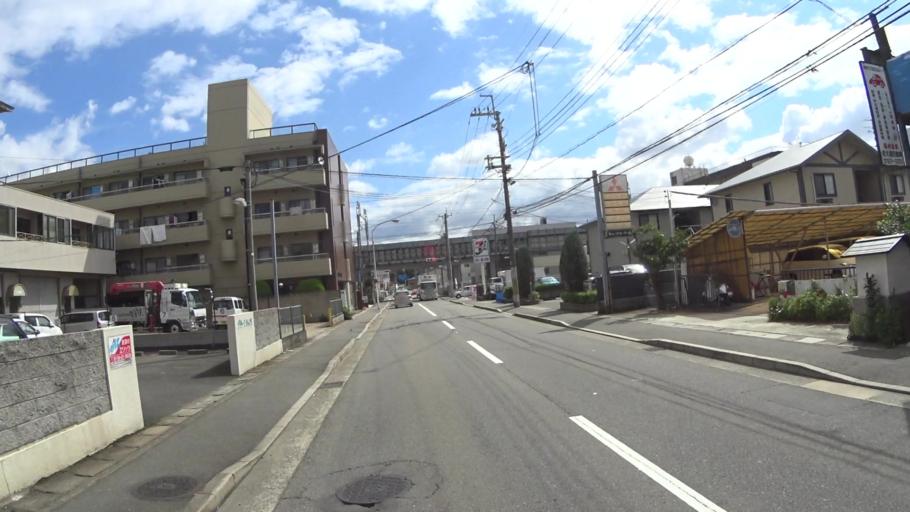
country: JP
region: Kyoto
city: Muko
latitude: 34.9596
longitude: 135.7134
